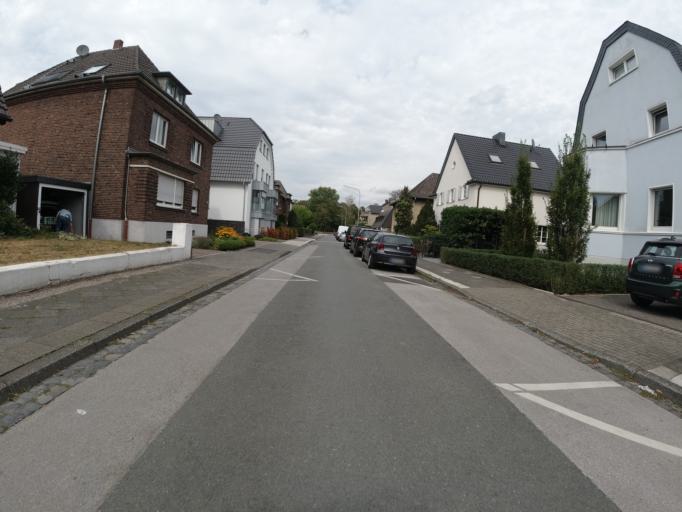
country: DE
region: North Rhine-Westphalia
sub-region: Regierungsbezirk Dusseldorf
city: Moers
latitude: 51.4444
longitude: 6.6227
